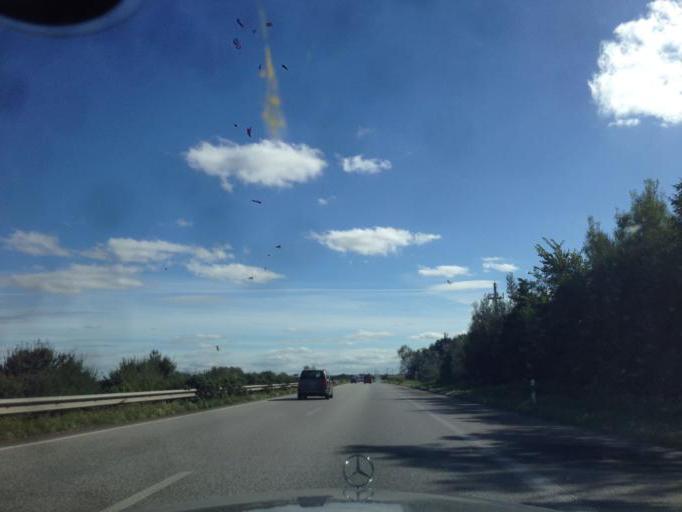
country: DE
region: Schleswig-Holstein
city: Sankelmark
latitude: 54.7010
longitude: 9.4033
